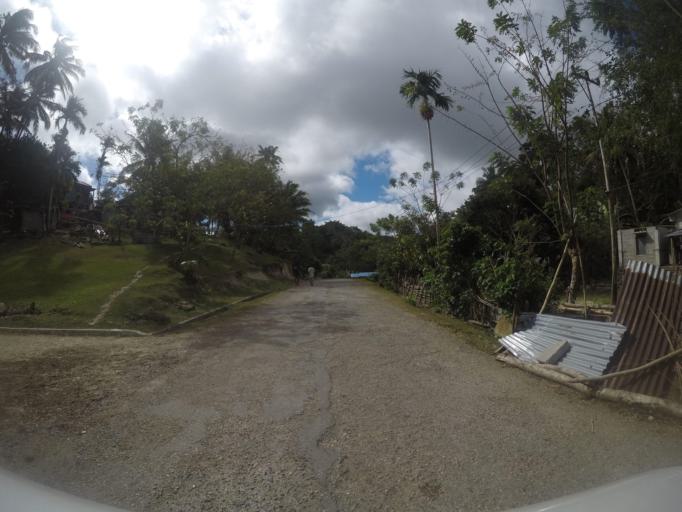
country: TL
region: Lautem
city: Lospalos
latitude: -8.5427
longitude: 126.9434
